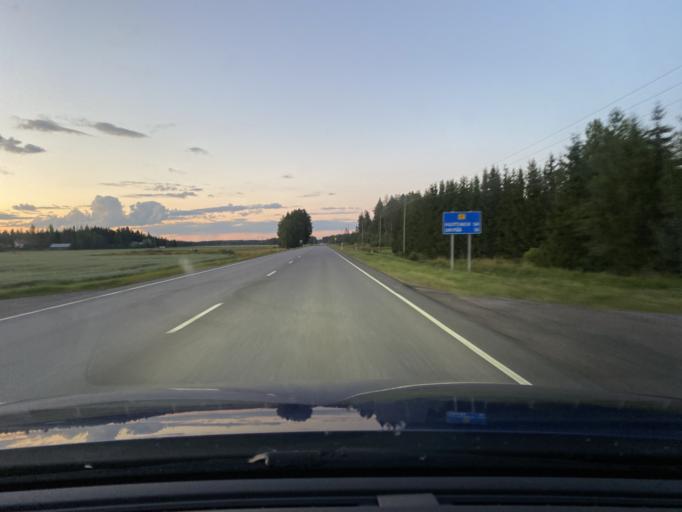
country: FI
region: Varsinais-Suomi
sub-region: Loimaa
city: Aura
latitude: 60.7278
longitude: 22.5833
